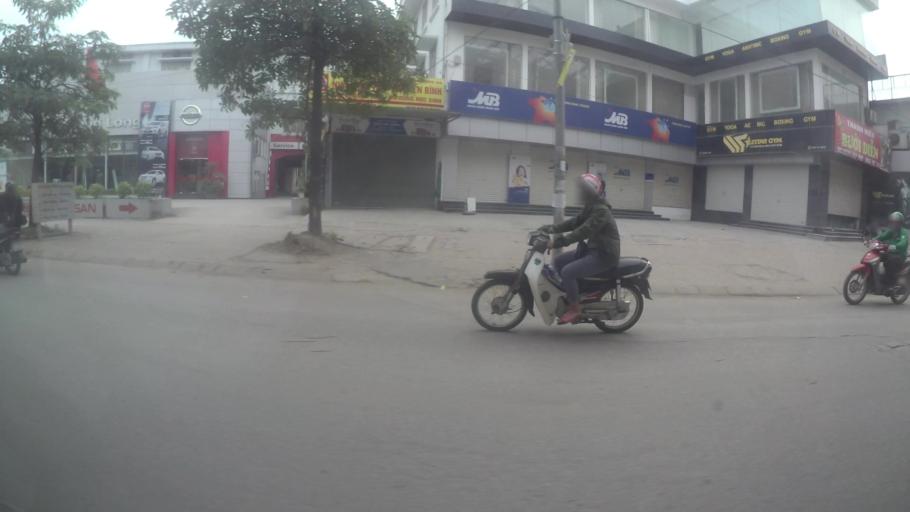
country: VN
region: Ha Noi
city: Cau Dien
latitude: 21.0477
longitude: 105.7453
